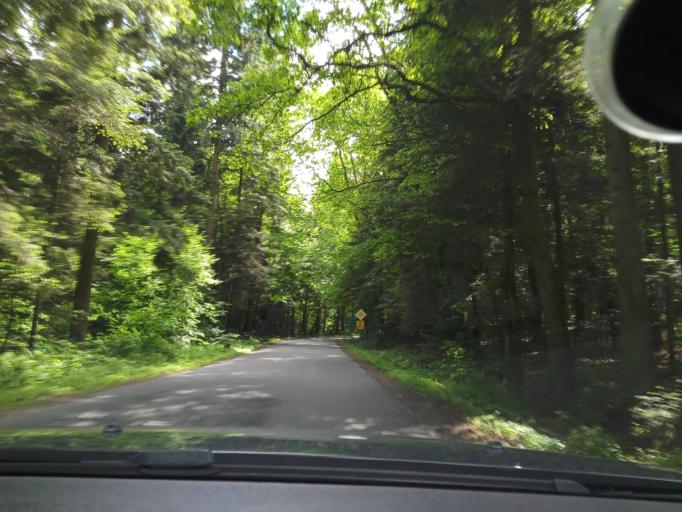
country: PL
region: Lesser Poland Voivodeship
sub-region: Powiat bochenski
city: Lapanow
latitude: 49.8621
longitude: 20.2496
